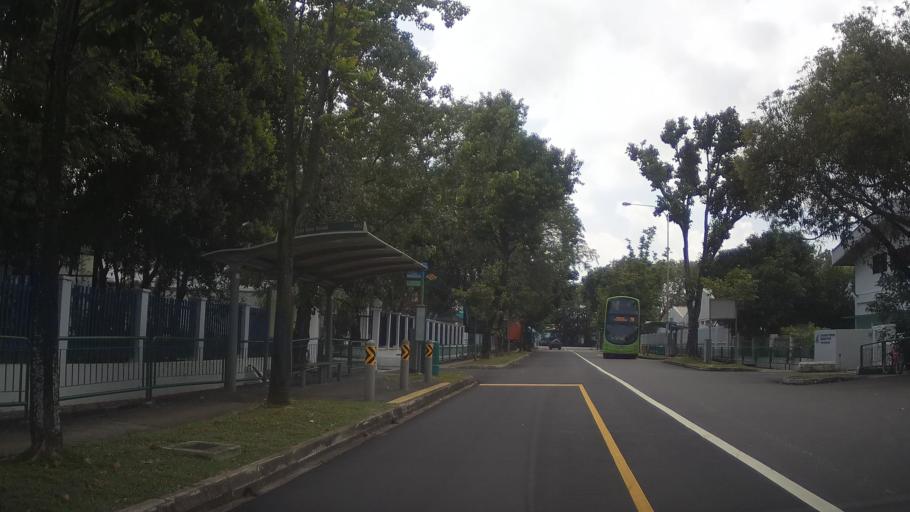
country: MY
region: Johor
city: Johor Bahru
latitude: 1.3320
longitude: 103.7162
